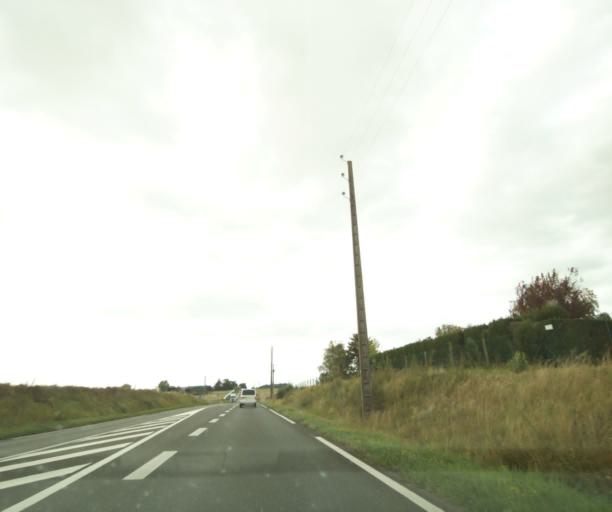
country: FR
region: Centre
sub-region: Departement d'Indre-et-Loire
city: Chambourg-sur-Indre
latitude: 47.1808
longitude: 0.9611
